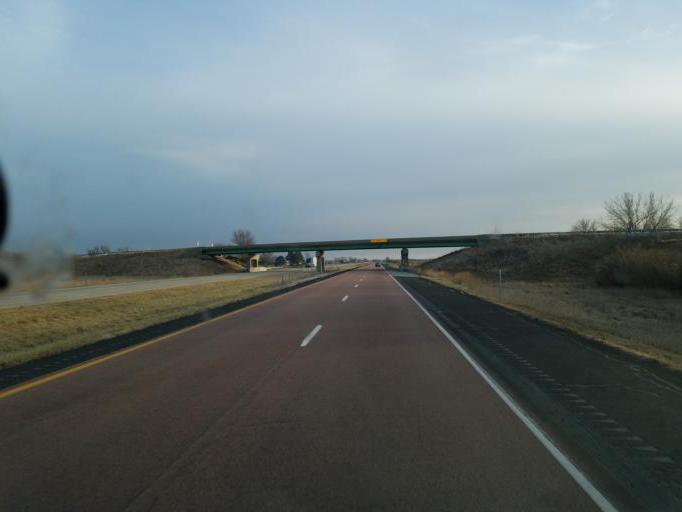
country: US
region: Iowa
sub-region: Monona County
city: Onawa
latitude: 42.0279
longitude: -96.1335
